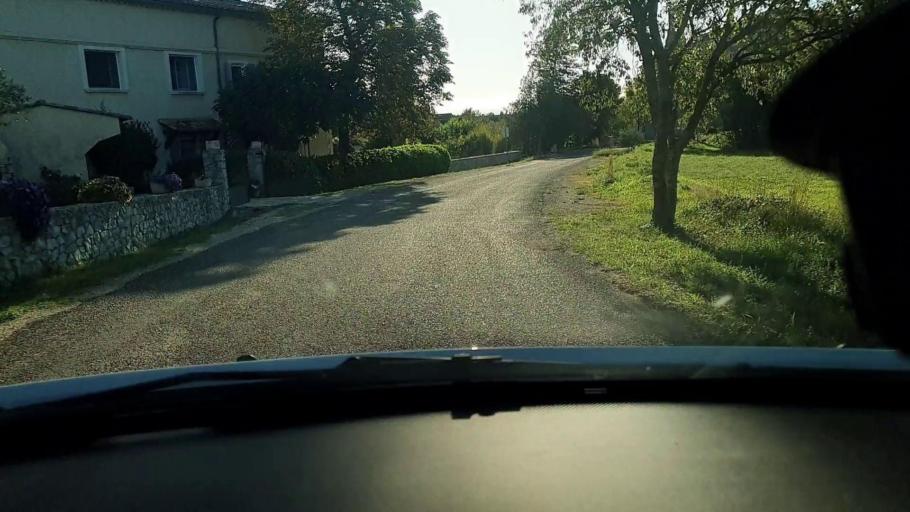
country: FR
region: Languedoc-Roussillon
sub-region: Departement du Gard
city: Barjac
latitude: 44.1860
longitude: 4.3262
